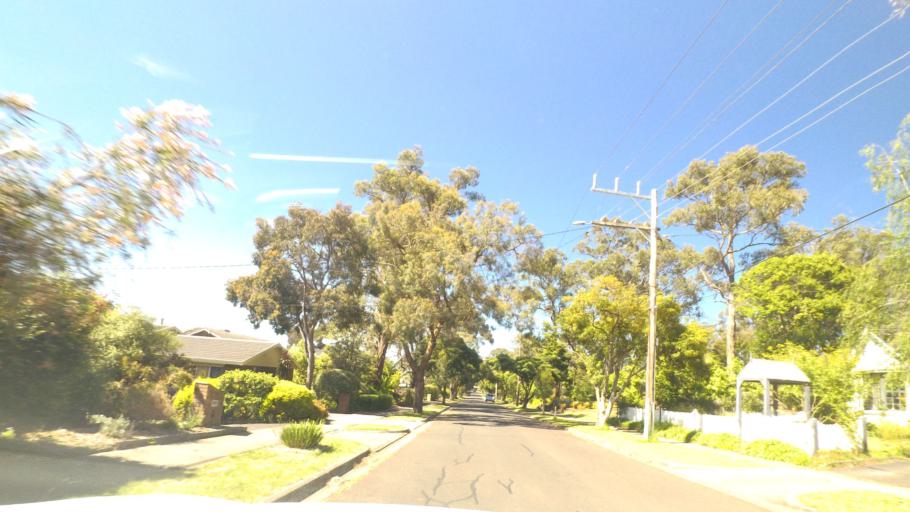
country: AU
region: Victoria
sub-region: Maroondah
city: Ringwood East
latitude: -37.8213
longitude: 145.2604
